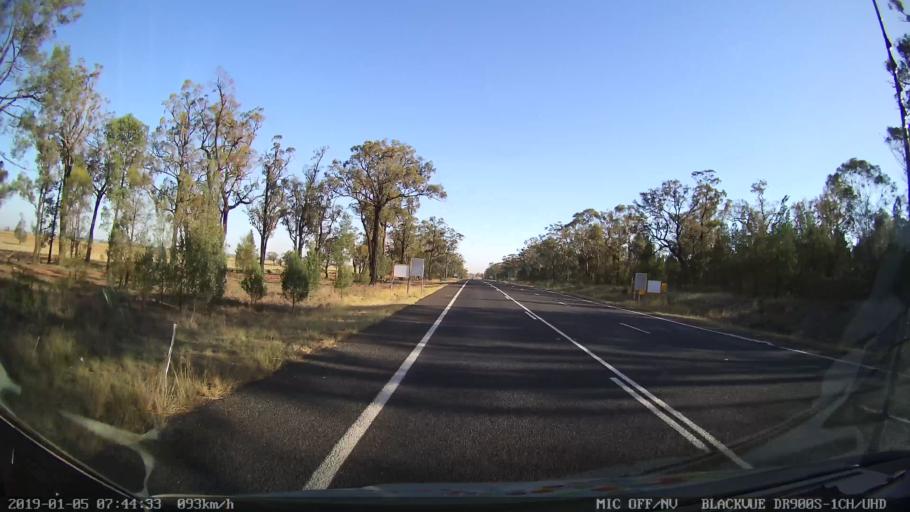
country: AU
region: New South Wales
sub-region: Gilgandra
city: Gilgandra
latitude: -31.8710
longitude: 148.6398
